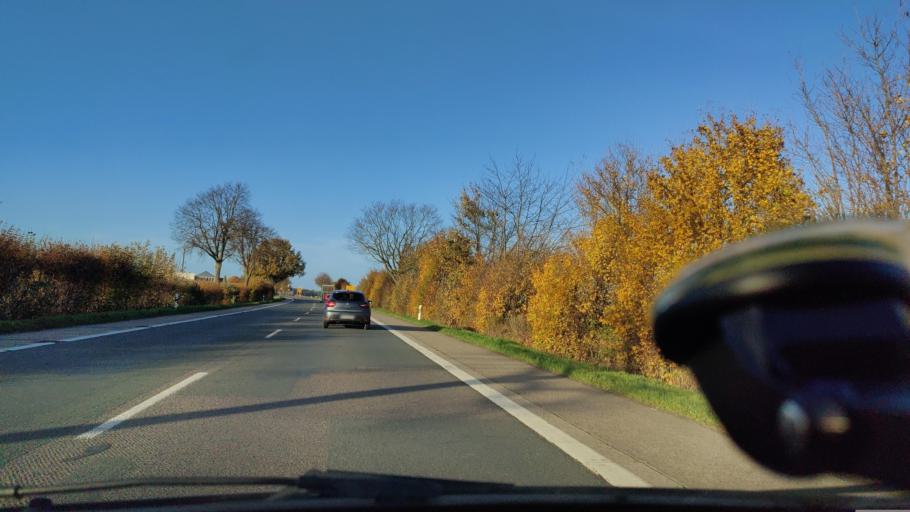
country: DE
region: North Rhine-Westphalia
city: Straelen
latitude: 51.4967
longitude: 6.2520
